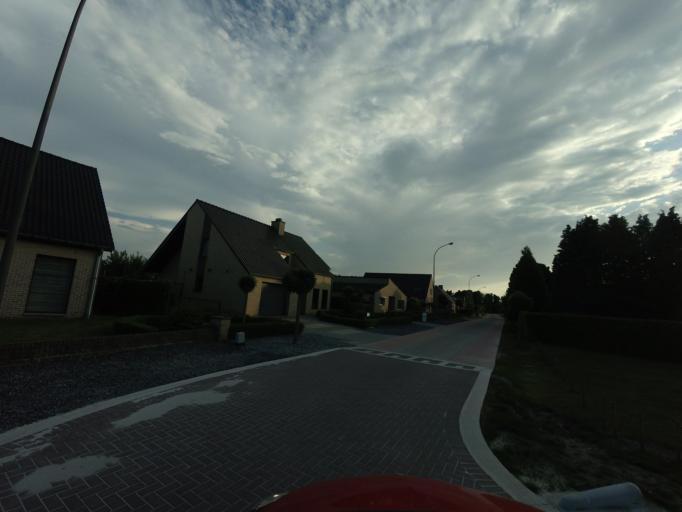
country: BE
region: Flanders
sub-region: Provincie Limburg
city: Lommel
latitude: 51.2330
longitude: 5.3270
